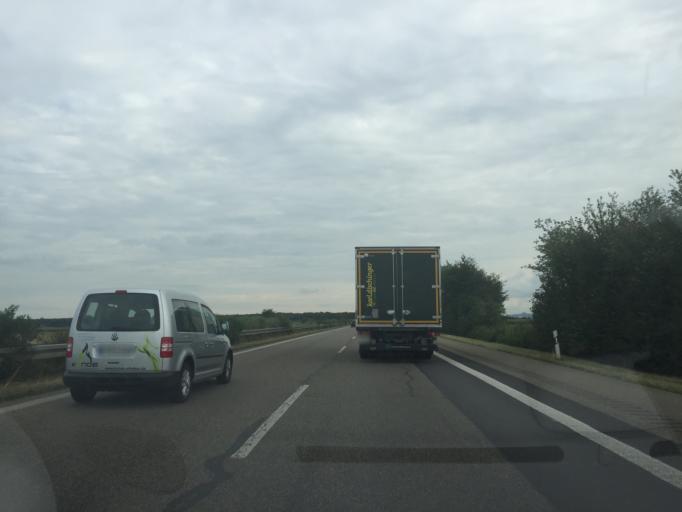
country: DE
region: Baden-Wuerttemberg
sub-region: Freiburg Region
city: Ringsheim
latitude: 48.2408
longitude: 7.7548
